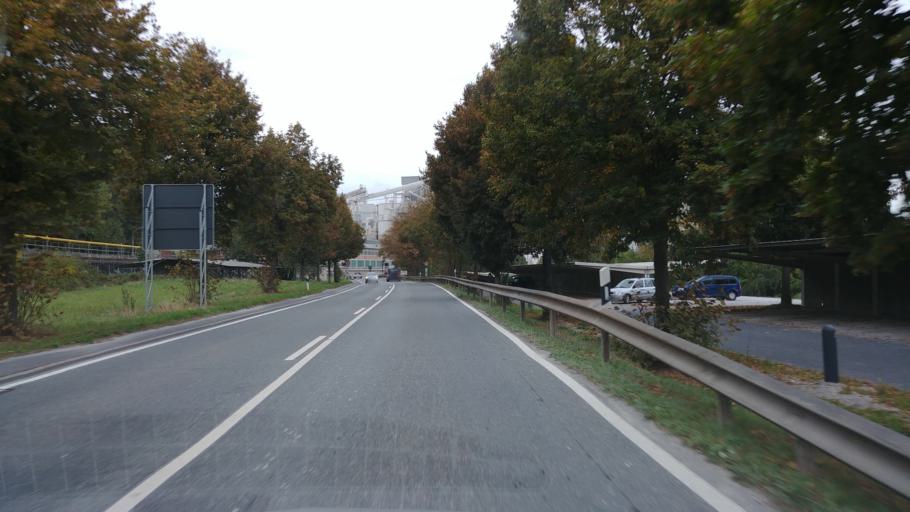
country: DE
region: Rheinland-Pfalz
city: Hahnstatten
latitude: 50.3145
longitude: 8.0660
